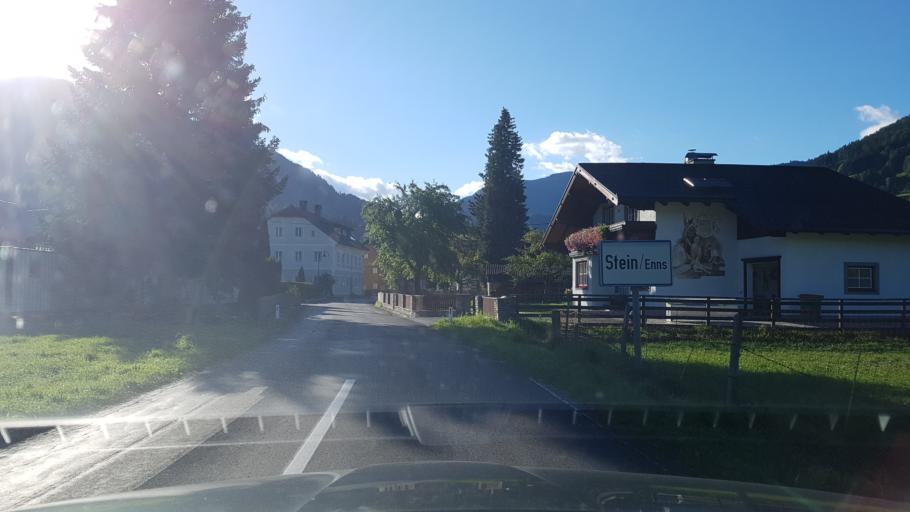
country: AT
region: Styria
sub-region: Politischer Bezirk Liezen
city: Grosssolk
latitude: 47.4393
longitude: 13.9388
